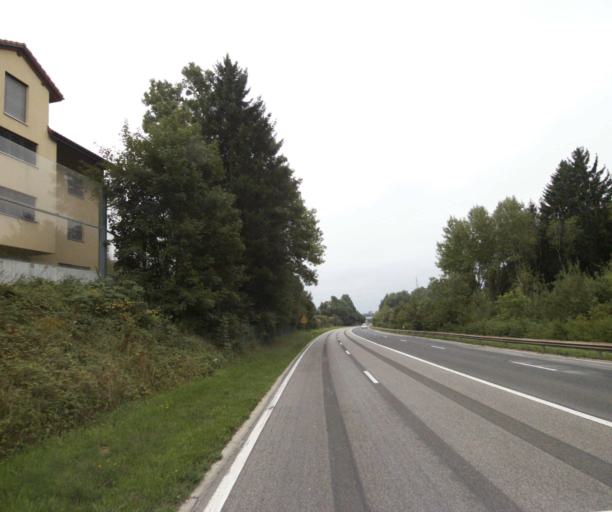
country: CH
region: Vaud
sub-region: Lausanne District
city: Epalinges
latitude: 46.5474
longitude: 6.6648
